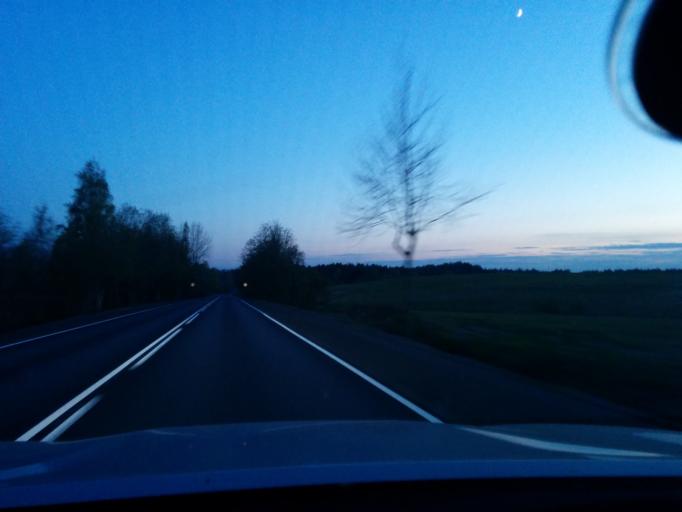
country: RU
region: Leningrad
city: Verkhniye Osel'ki
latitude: 60.1845
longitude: 30.3970
